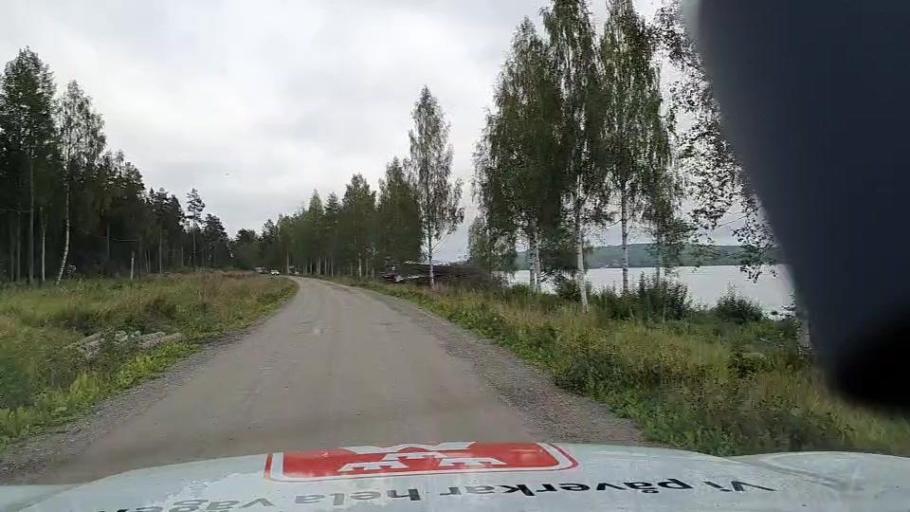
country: SE
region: Jaemtland
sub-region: Ragunda Kommun
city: Hammarstrand
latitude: 63.1695
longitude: 15.8229
